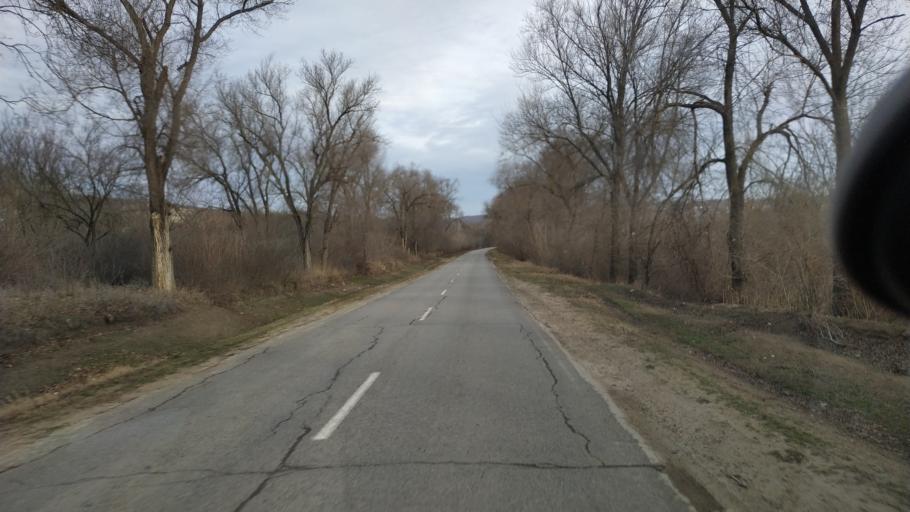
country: MD
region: Chisinau
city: Vadul lui Voda
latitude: 47.1270
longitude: 29.0633
